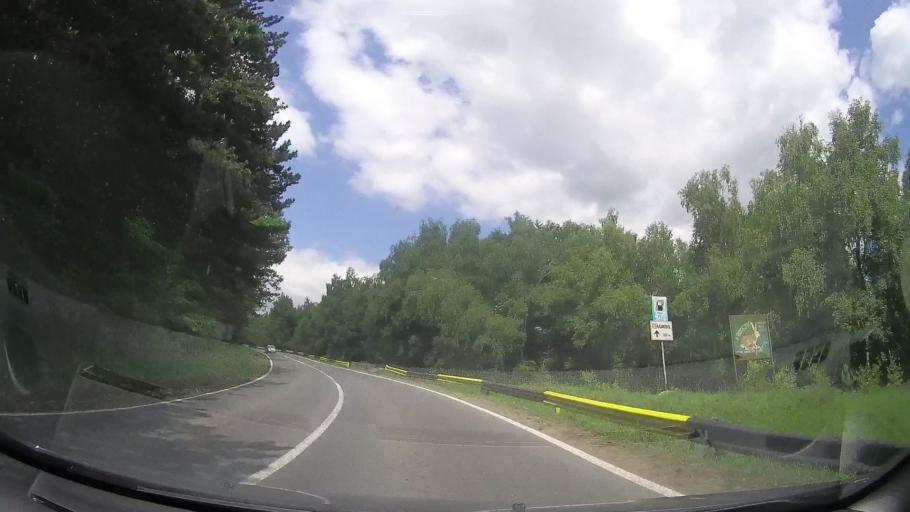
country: RO
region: Prahova
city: Maneciu
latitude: 45.3301
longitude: 25.9748
